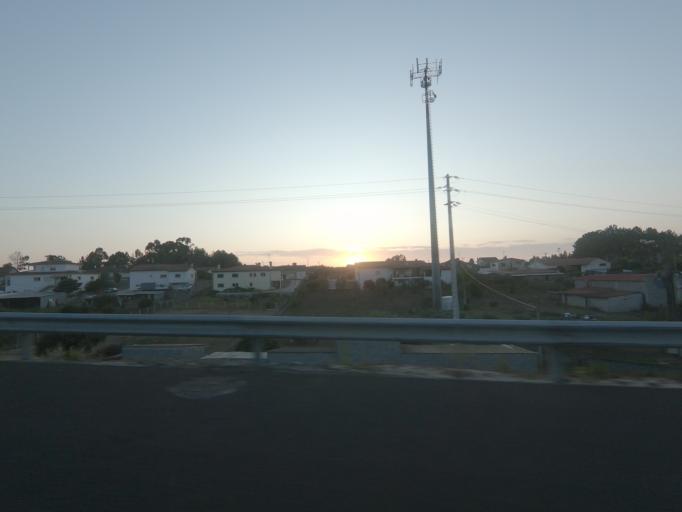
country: PT
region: Leiria
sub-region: Pombal
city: Pombal
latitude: 39.9025
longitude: -8.6894
